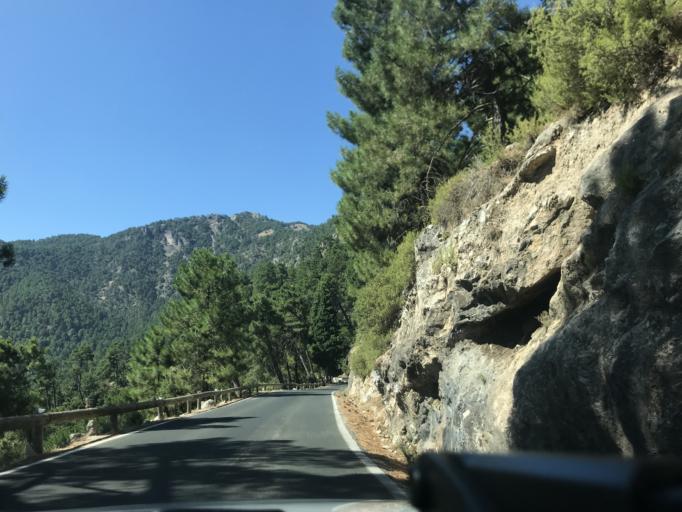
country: ES
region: Andalusia
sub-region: Provincia de Jaen
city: La Iruela
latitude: 37.9258
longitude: -2.9507
